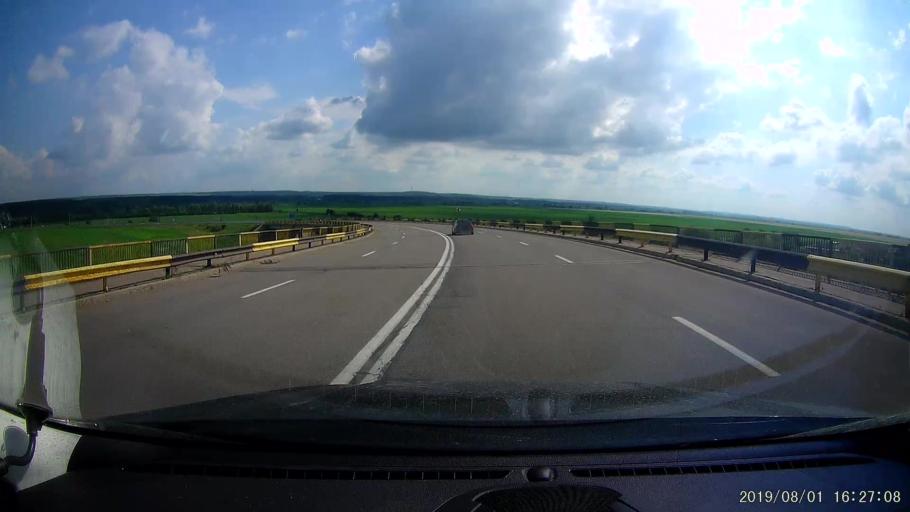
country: RO
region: Calarasi
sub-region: Municipiul Calarasi
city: Calarasi
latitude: 44.1677
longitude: 27.3114
